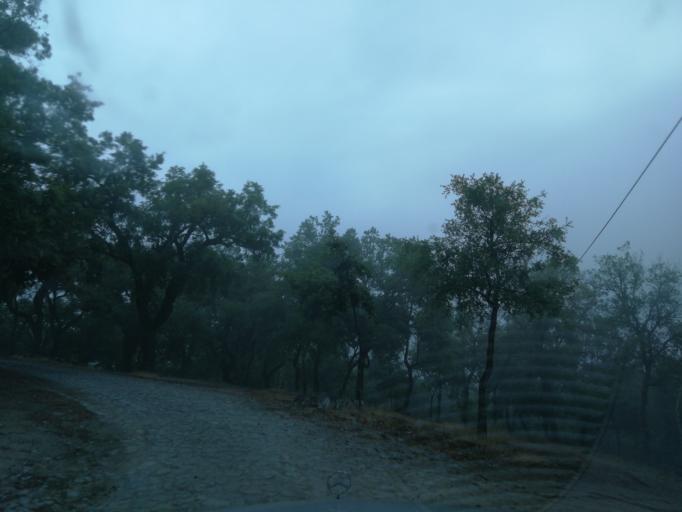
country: PT
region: Braga
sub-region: Braga
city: Braga
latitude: 41.5216
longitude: -8.3873
